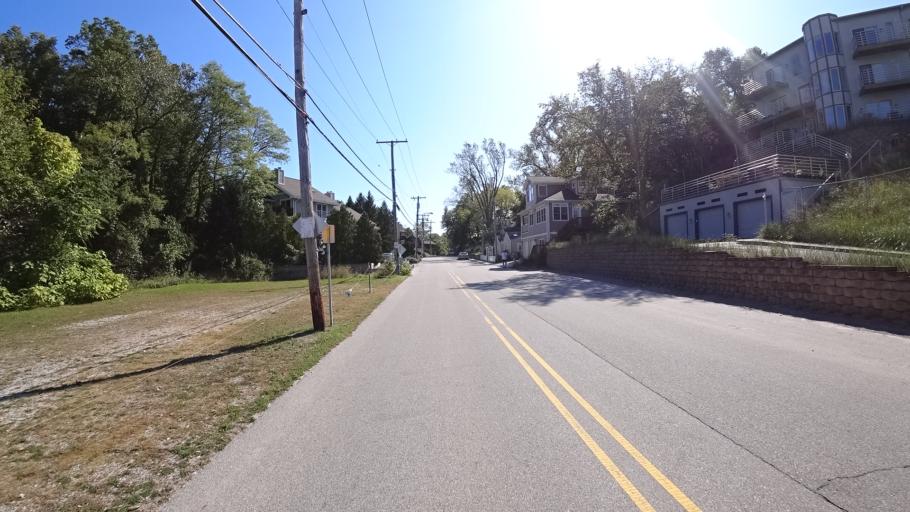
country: US
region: Indiana
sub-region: LaPorte County
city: Michigan City
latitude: 41.7287
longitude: -86.8915
